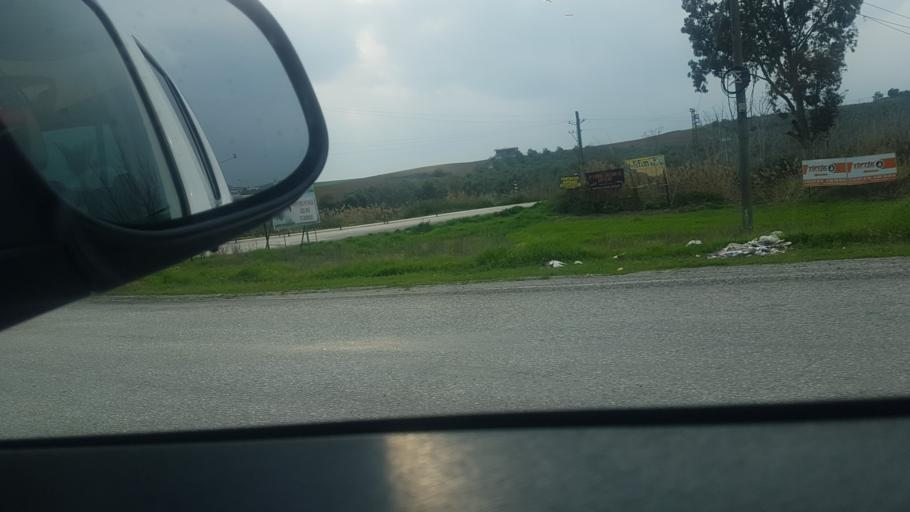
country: TR
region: Mersin
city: Yenice
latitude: 37.0568
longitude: 35.1681
